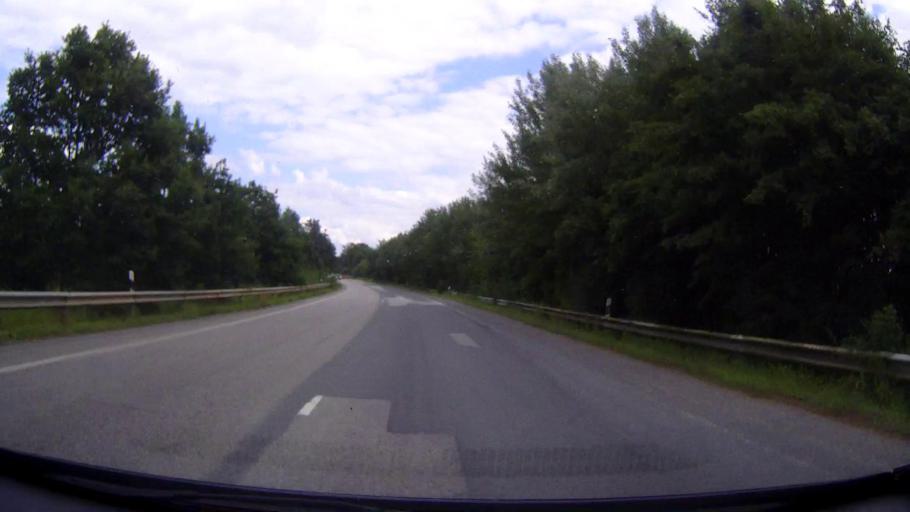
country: DE
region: Schleswig-Holstein
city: Badendorf
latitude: 53.8940
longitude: 10.6002
